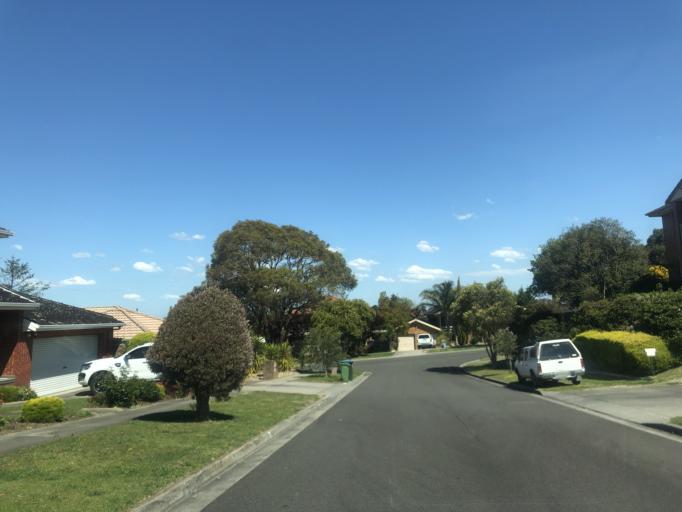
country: AU
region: Victoria
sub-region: Casey
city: Endeavour Hills
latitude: -37.9887
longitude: 145.2681
